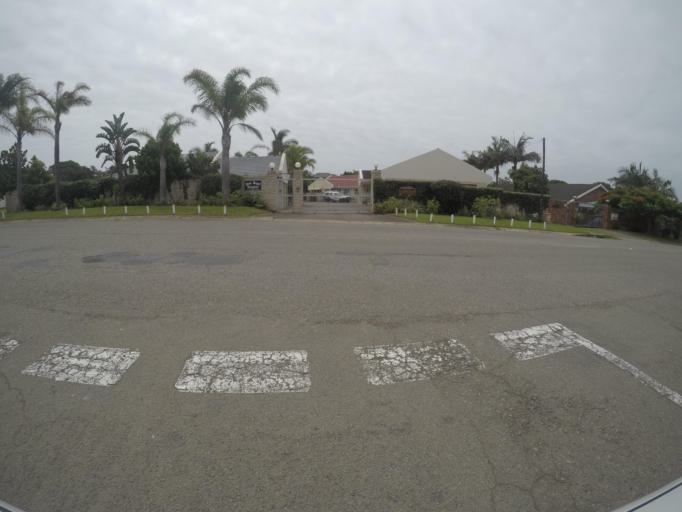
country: ZA
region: Eastern Cape
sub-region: Buffalo City Metropolitan Municipality
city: East London
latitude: -32.9787
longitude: 27.9504
